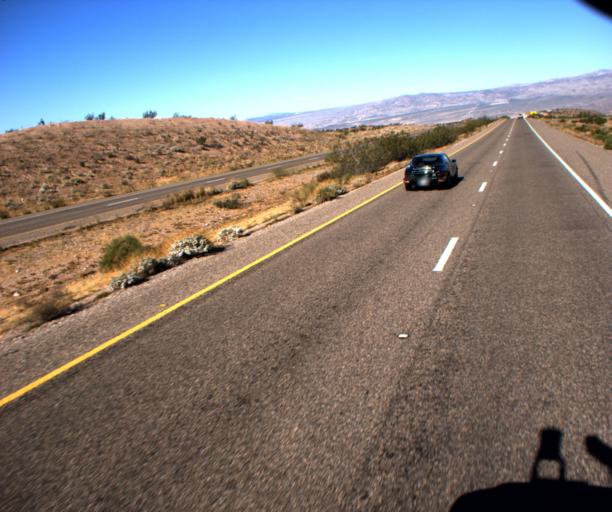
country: US
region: Nevada
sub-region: Clark County
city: Laughlin
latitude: 35.1855
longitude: -114.4806
